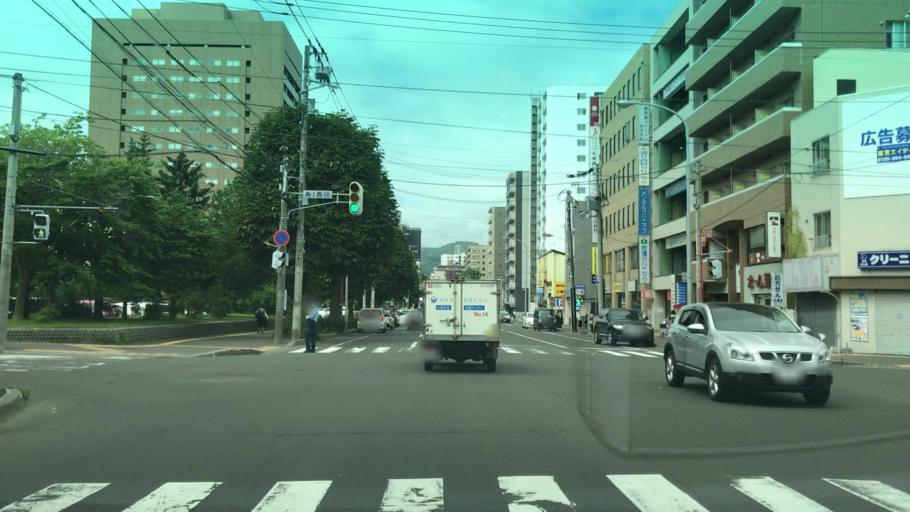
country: JP
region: Hokkaido
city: Sapporo
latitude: 43.0565
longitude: 141.3340
